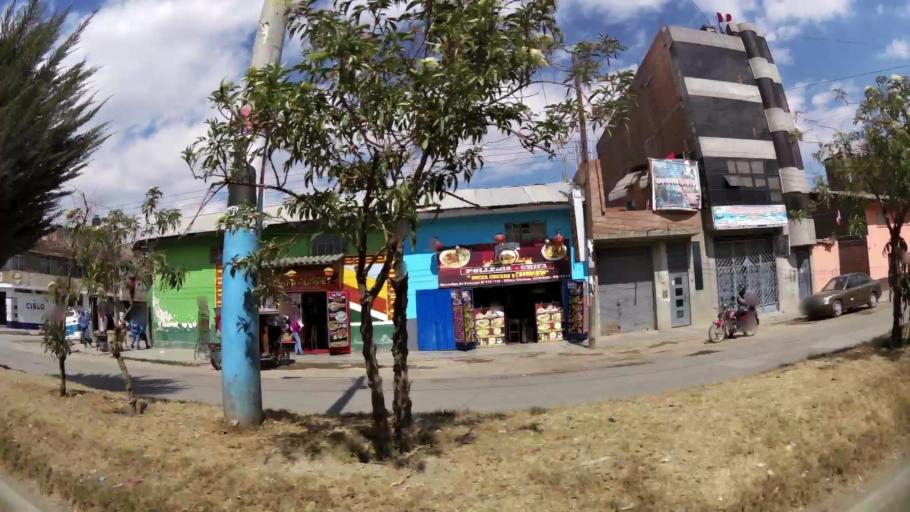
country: PE
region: Junin
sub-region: Provincia de Huancayo
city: Huancayo
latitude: -12.0868
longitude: -75.2009
